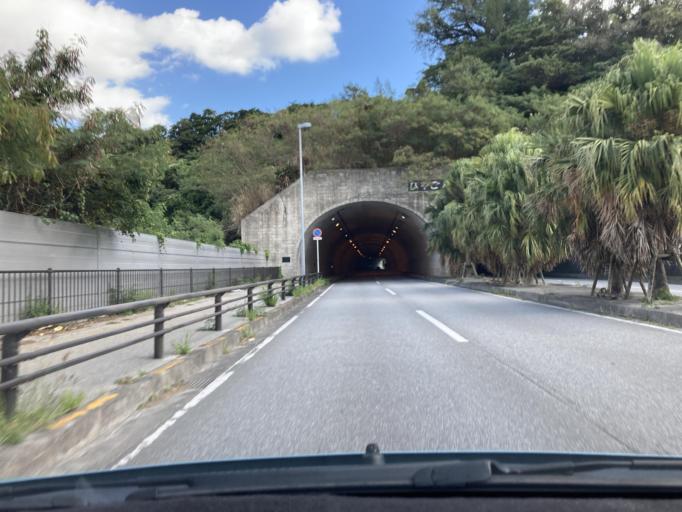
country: JP
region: Okinawa
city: Okinawa
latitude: 26.3160
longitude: 127.8100
